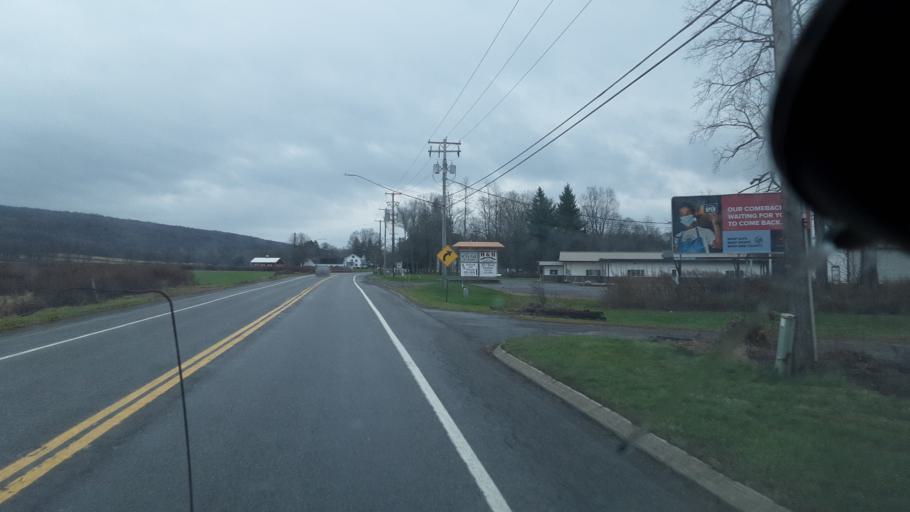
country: US
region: New York
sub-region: Erie County
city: Holland
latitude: 42.6824
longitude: -78.5648
